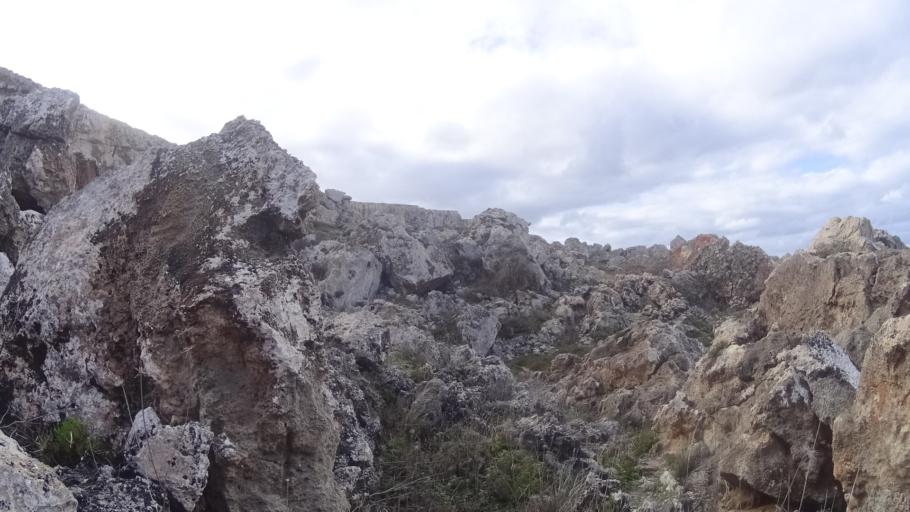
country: MT
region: Il-Mellieha
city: Mellieha
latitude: 35.9793
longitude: 14.3281
